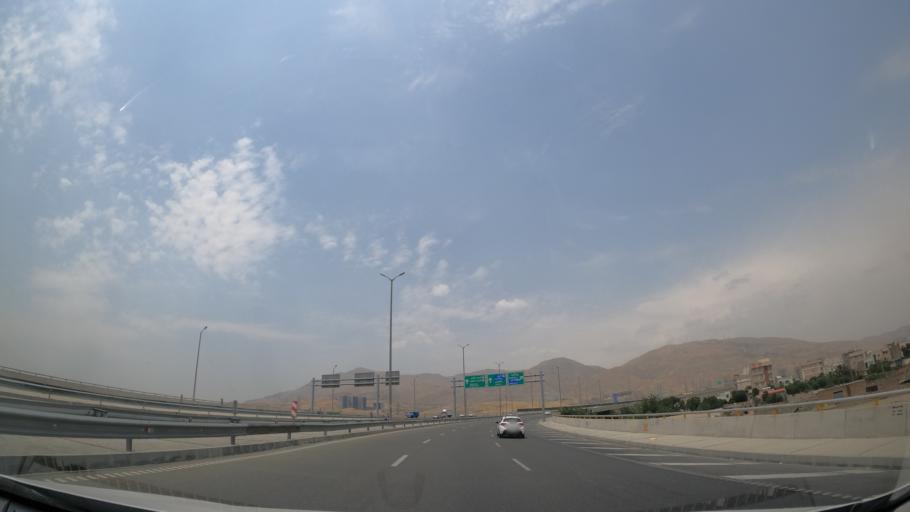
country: IR
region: Tehran
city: Shahr-e Qods
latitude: 35.7367
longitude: 51.1216
